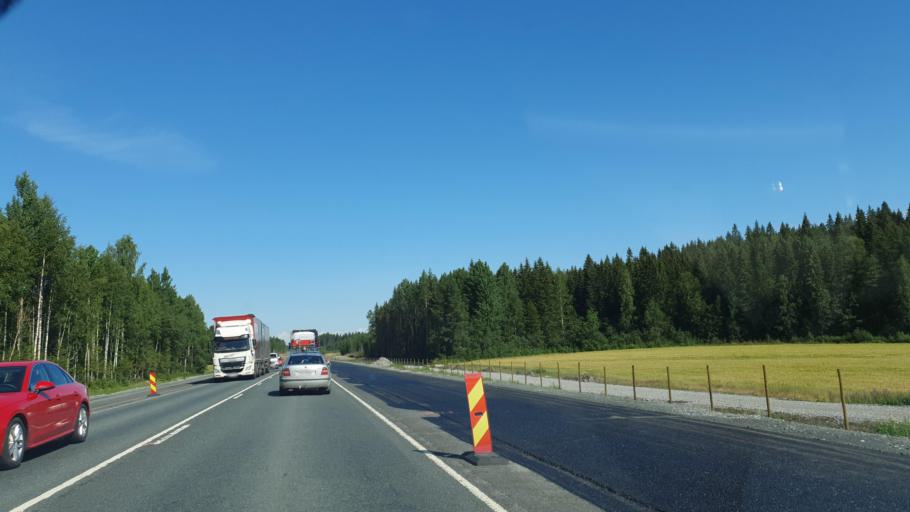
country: FI
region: Northern Savo
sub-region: Ylae-Savo
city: Lapinlahti
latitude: 63.2924
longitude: 27.4538
